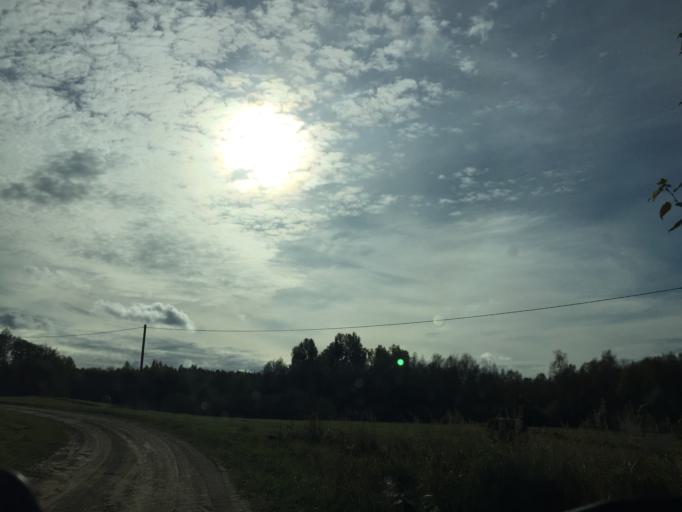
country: LV
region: Jaunpils
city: Jaunpils
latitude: 56.6067
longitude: 22.9976
